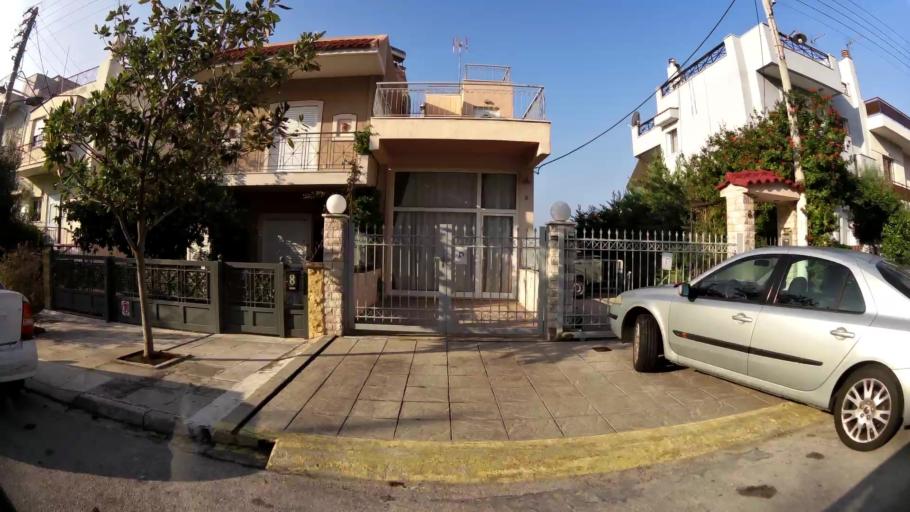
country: GR
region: Attica
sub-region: Nomarchia Athinas
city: Ilioupoli
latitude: 37.9357
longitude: 23.7539
